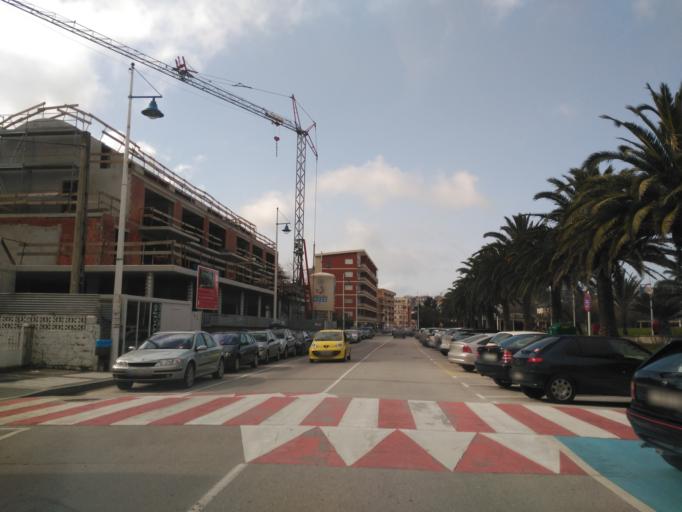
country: ES
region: Cantabria
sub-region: Provincia de Cantabria
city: Suances
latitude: 43.4338
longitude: -4.0384
